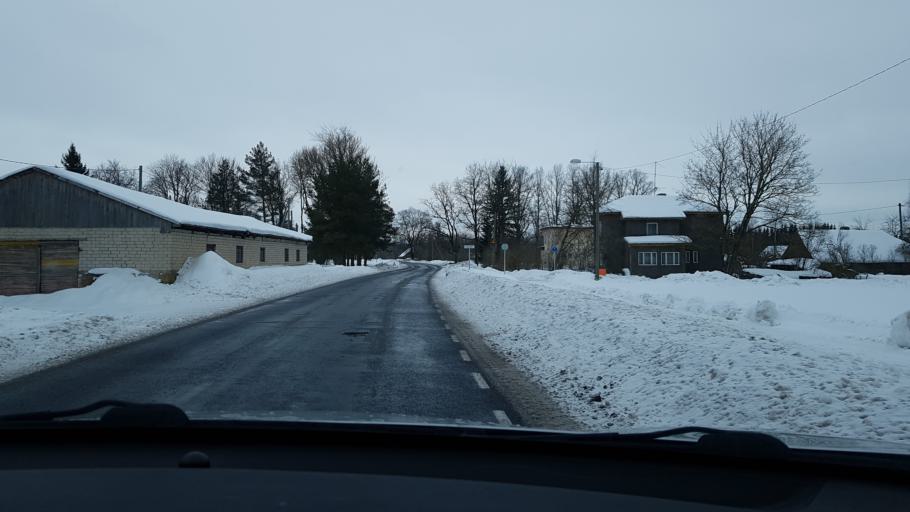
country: EE
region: Jaervamaa
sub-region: Jaerva-Jaani vald
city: Jarva-Jaani
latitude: 59.1503
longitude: 25.7524
